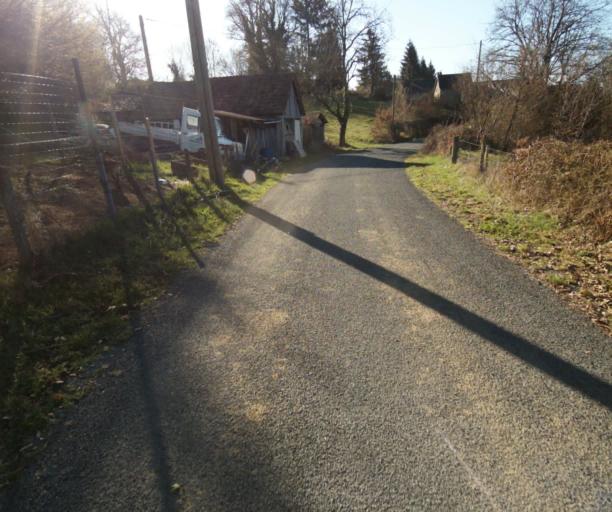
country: FR
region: Limousin
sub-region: Departement de la Correze
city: Seilhac
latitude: 45.3655
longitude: 1.7566
